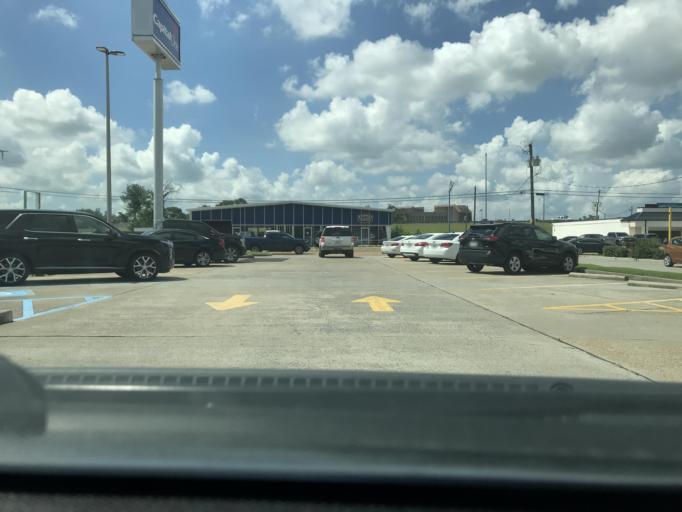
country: US
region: Louisiana
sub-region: Calcasieu Parish
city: Lake Charles
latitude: 30.1987
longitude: -93.2177
